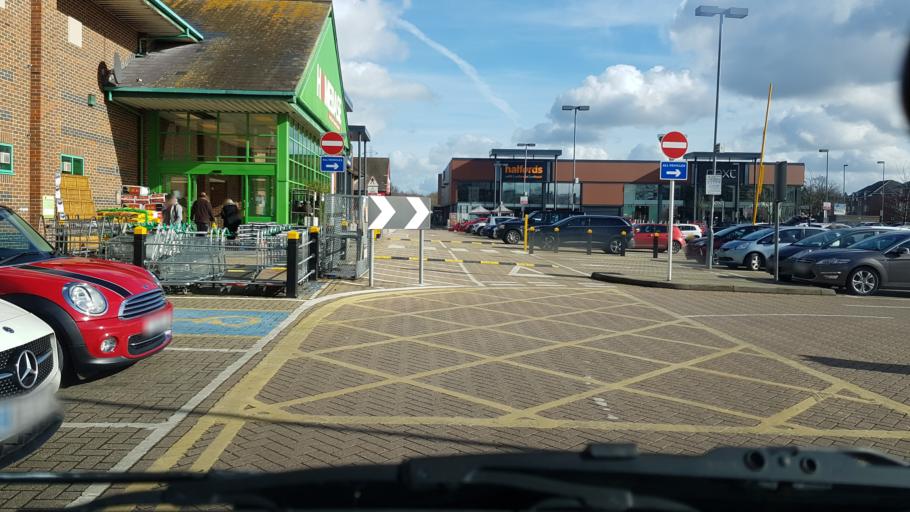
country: GB
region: England
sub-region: Surrey
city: Guildford
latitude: 51.2484
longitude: -0.5793
